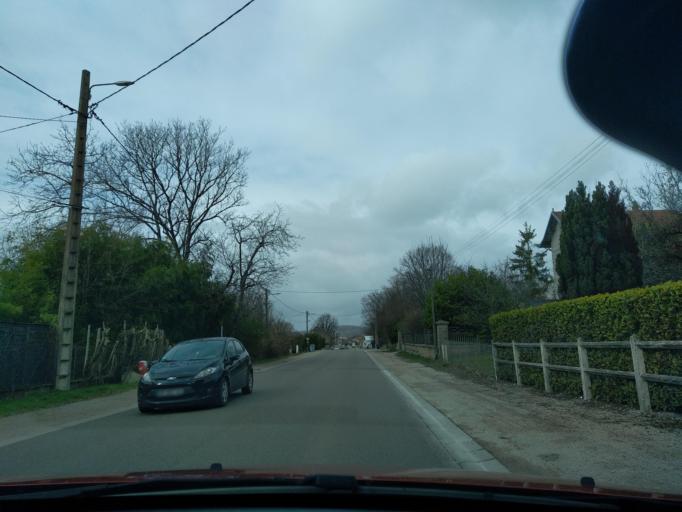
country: FR
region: Franche-Comte
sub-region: Departement du Jura
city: Perrigny
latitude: 46.6638
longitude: 5.5846
